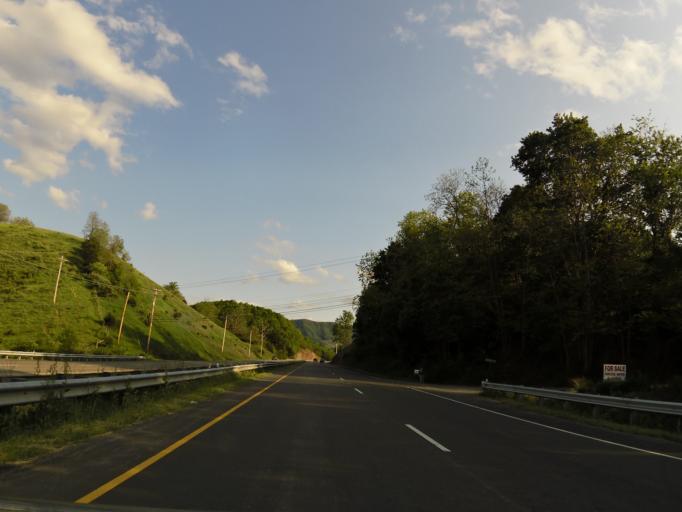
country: US
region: Virginia
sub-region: Tazewell County
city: Claypool Hill
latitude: 37.0283
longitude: -81.7978
